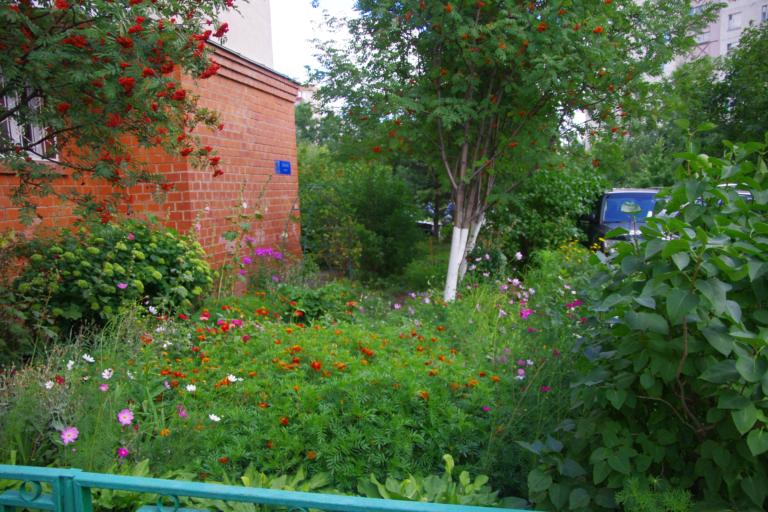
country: RU
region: Moskovskaya
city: Krasnogorsk
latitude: 55.8324
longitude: 37.2997
